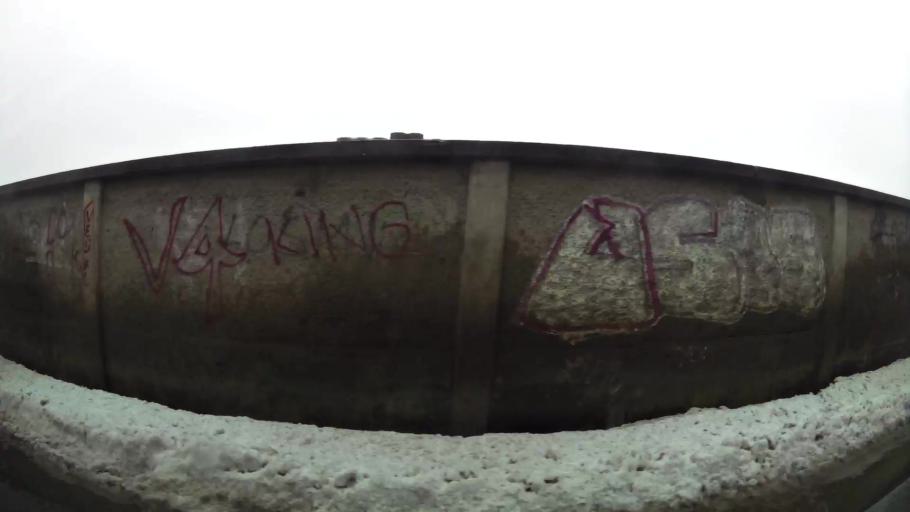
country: RS
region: Central Serbia
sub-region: Belgrade
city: Zemun
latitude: 44.8479
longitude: 20.3604
